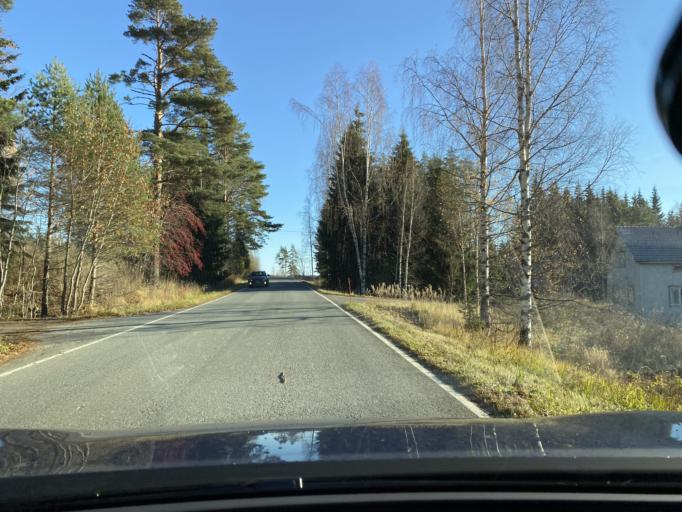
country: FI
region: Pirkanmaa
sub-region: Etelae-Pirkanmaa
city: Akaa
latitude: 61.0110
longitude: 23.9003
